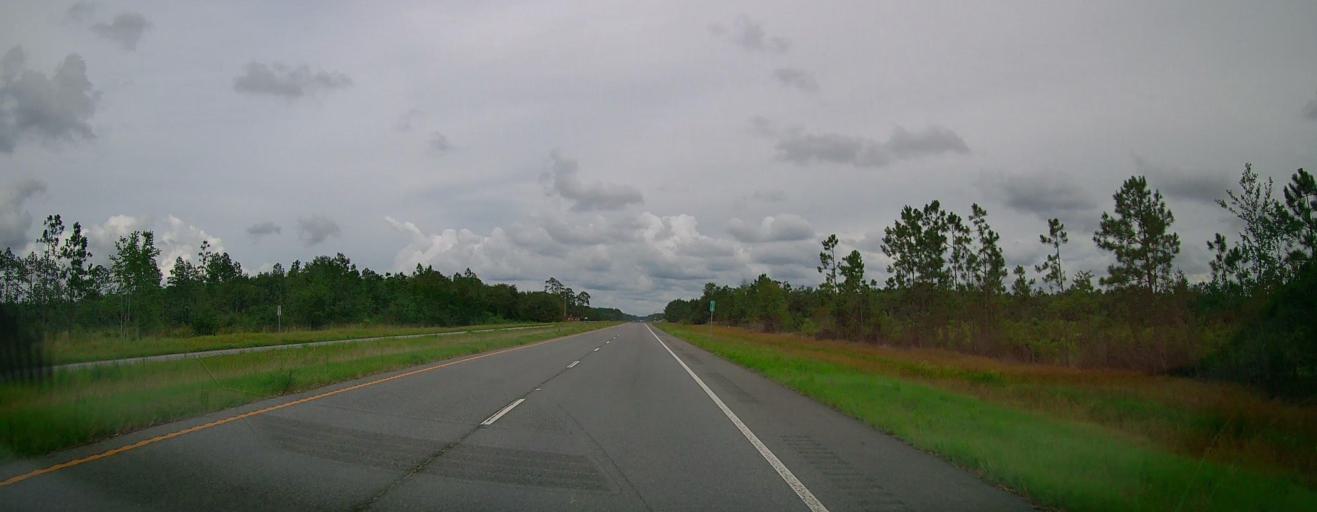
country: US
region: Georgia
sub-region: Appling County
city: Baxley
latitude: 31.7400
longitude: -82.2382
